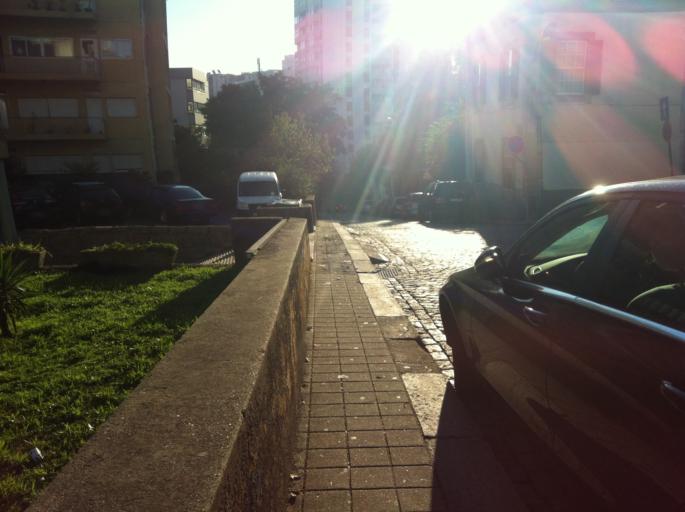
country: PT
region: Porto
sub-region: Porto
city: Porto
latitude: 41.1517
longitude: -8.6305
